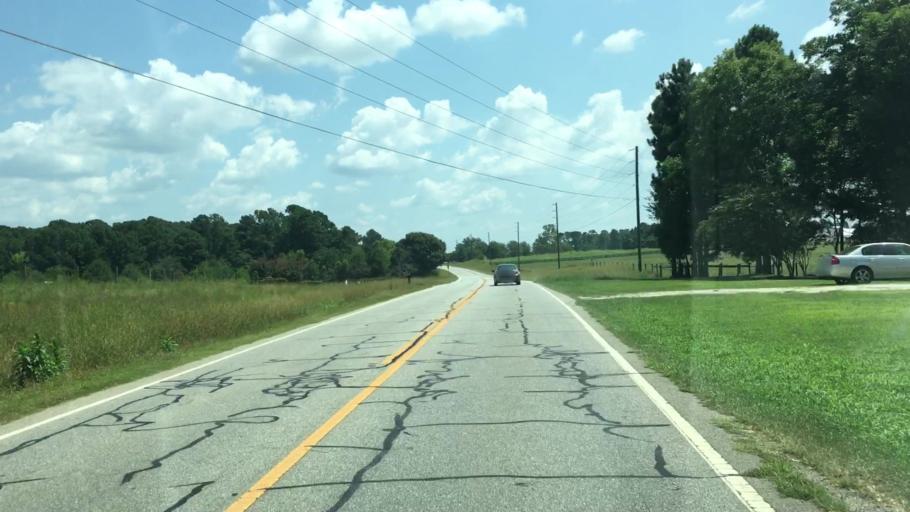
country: US
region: Georgia
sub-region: Barrow County
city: Statham
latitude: 33.9484
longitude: -83.6495
